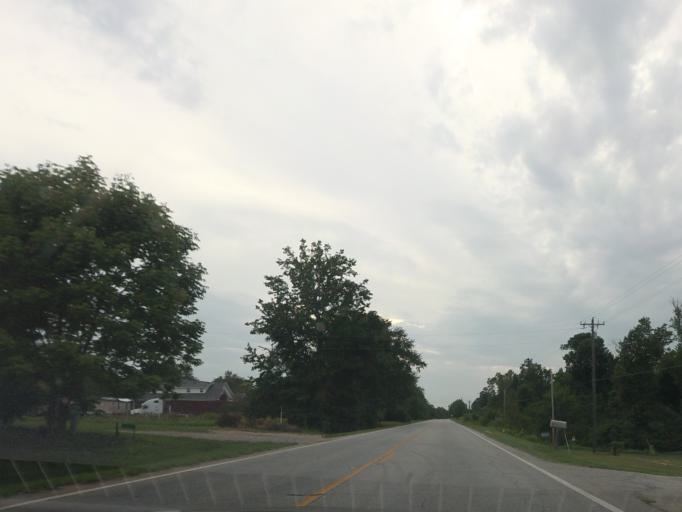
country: US
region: Georgia
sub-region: Twiggs County
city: Jeffersonville
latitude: 32.7614
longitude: -83.4511
